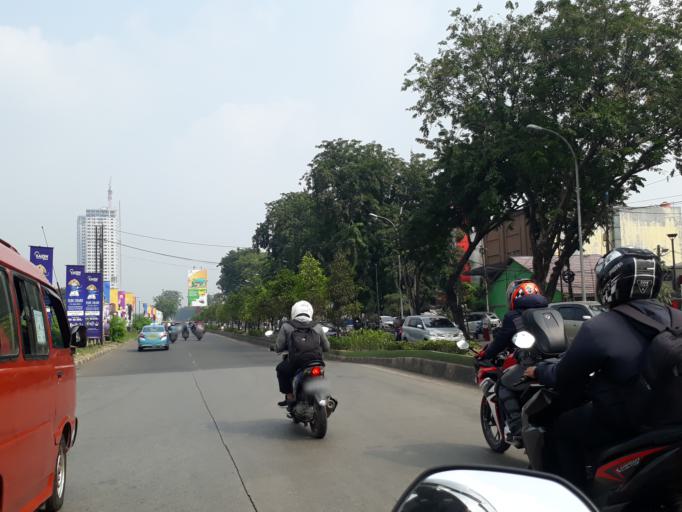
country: ID
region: West Java
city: Bekasi
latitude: -6.2483
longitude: 106.9838
